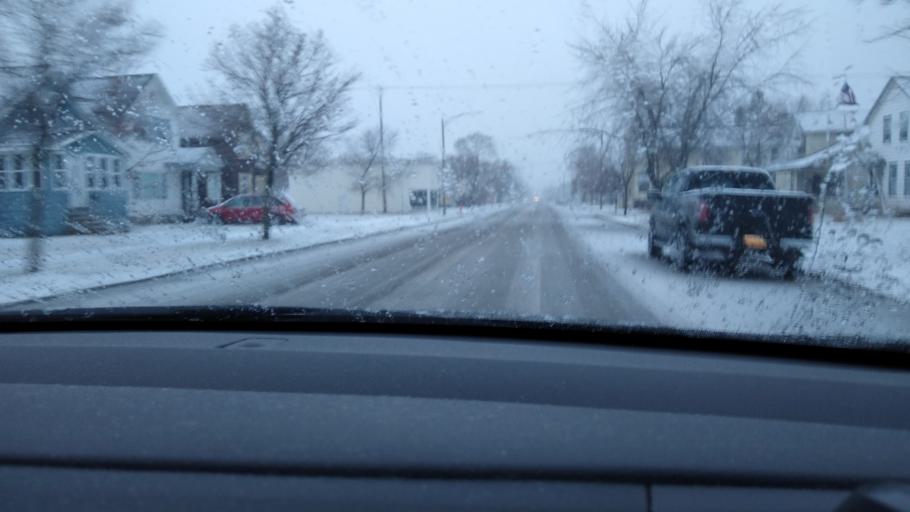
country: US
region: Michigan
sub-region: Delta County
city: Escanaba
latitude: 45.7402
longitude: -87.0612
